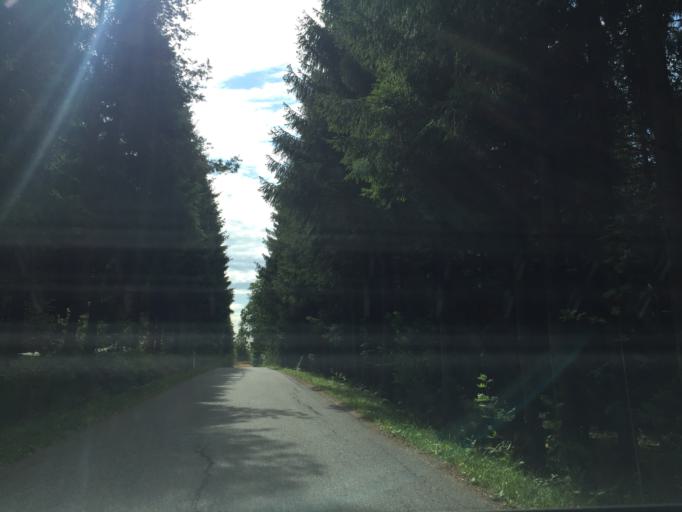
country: NO
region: Akershus
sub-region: Ski
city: Ski
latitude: 59.6532
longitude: 10.8720
